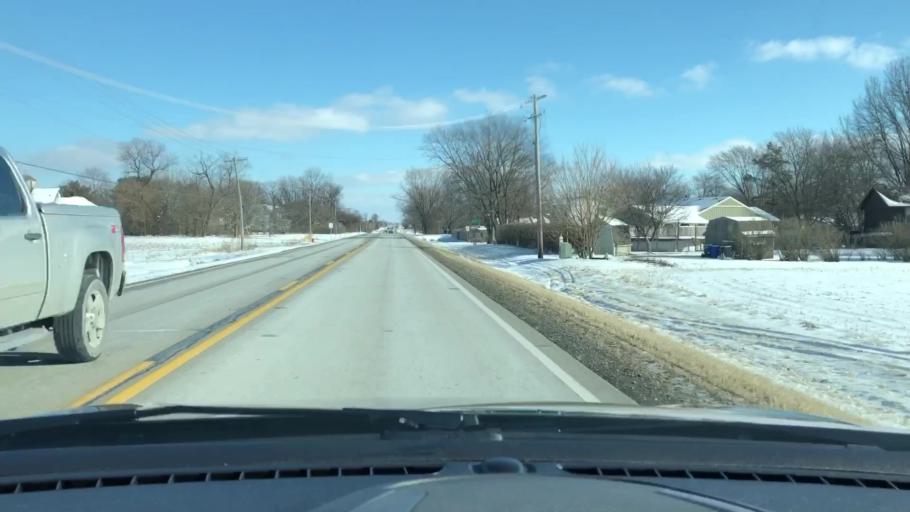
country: US
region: Illinois
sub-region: Will County
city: New Lenox
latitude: 41.4825
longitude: -87.9990
